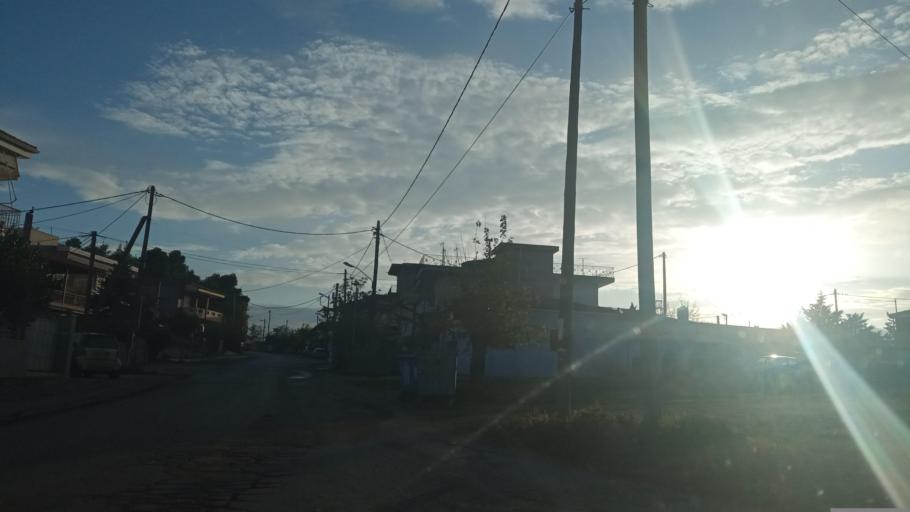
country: GR
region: Central Greece
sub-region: Nomos Evvoias
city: Psachna
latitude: 38.5842
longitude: 23.7137
